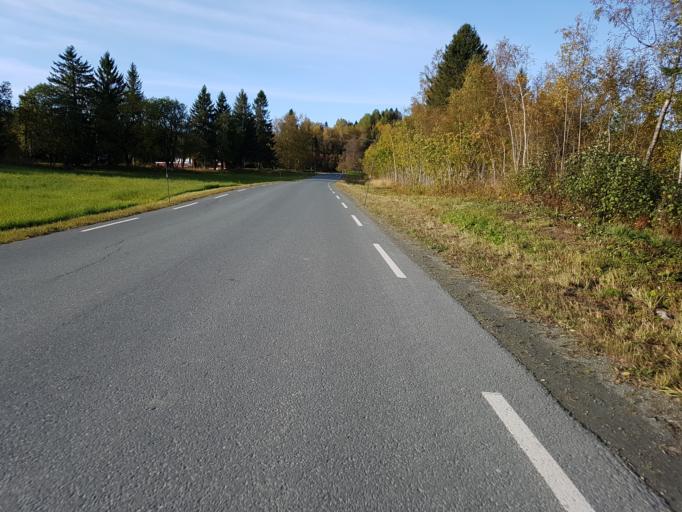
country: NO
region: Sor-Trondelag
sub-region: Klaebu
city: Klaebu
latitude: 63.3454
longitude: 10.5155
